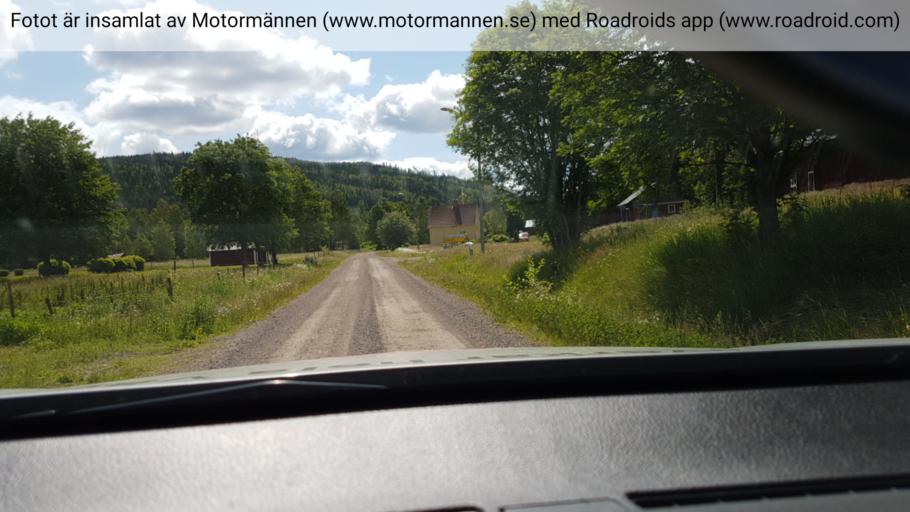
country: SE
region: Vaermland
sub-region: Hagfors Kommun
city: Ekshaerad
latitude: 60.3256
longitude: 13.3730
